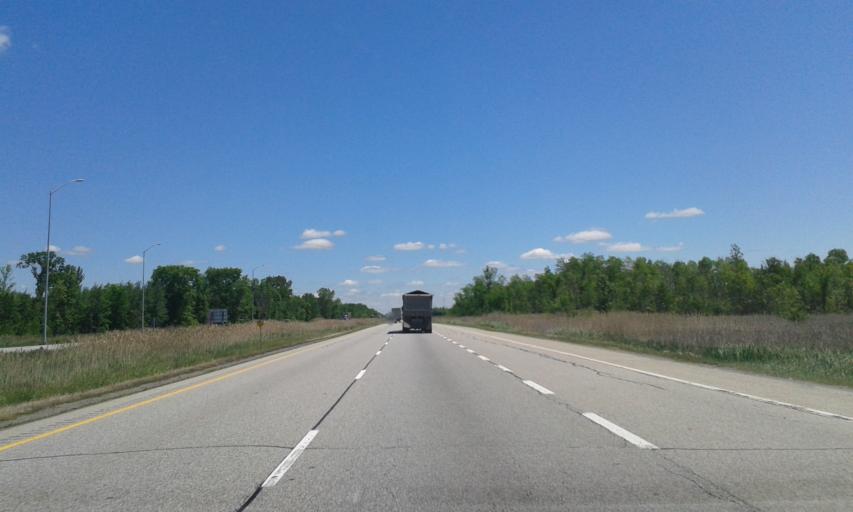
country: US
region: New York
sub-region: St. Lawrence County
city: Norfolk
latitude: 44.9174
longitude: -75.1963
